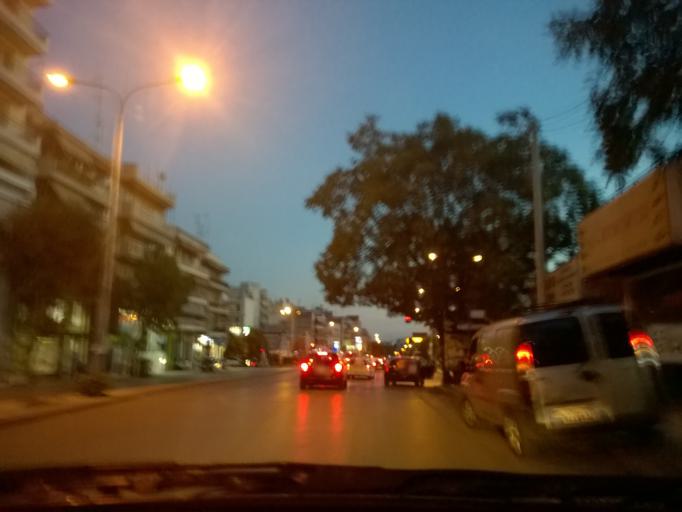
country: GR
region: Central Macedonia
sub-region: Nomos Thessalonikis
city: Thessaloniki
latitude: 40.6490
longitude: 22.9354
